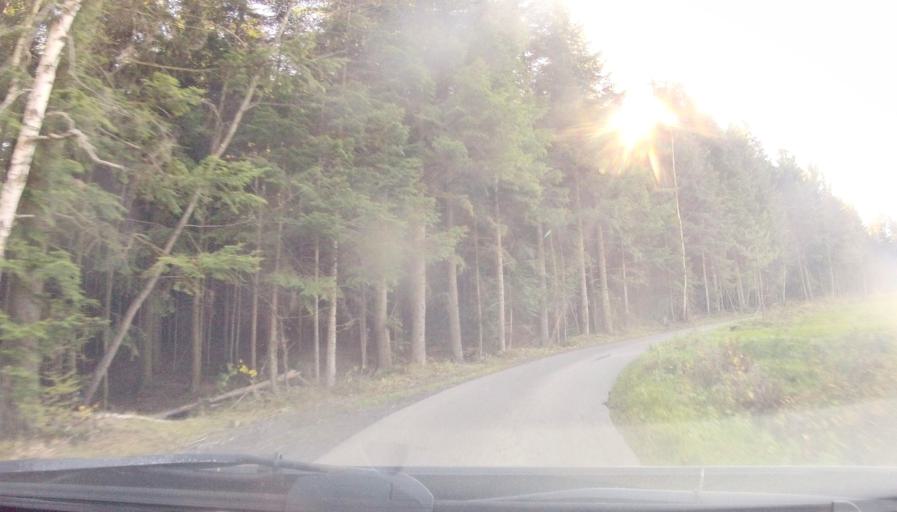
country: PL
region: Lesser Poland Voivodeship
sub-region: Powiat suski
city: Krzeszow
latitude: 49.7607
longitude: 19.4493
